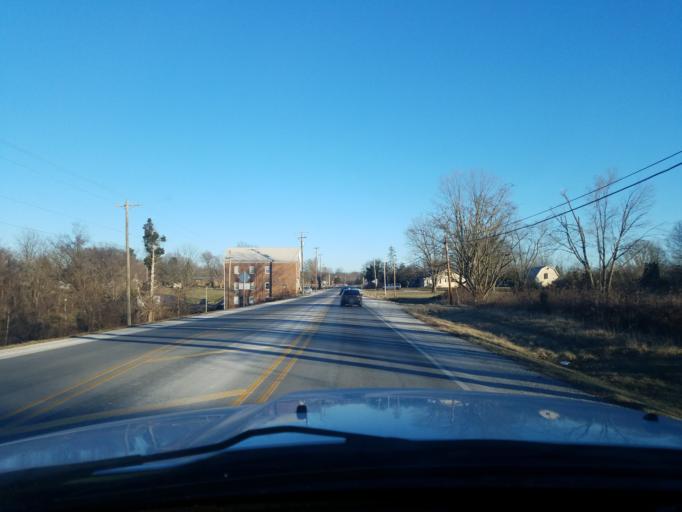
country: US
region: Indiana
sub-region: Floyd County
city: Galena
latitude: 38.3507
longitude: -85.9366
